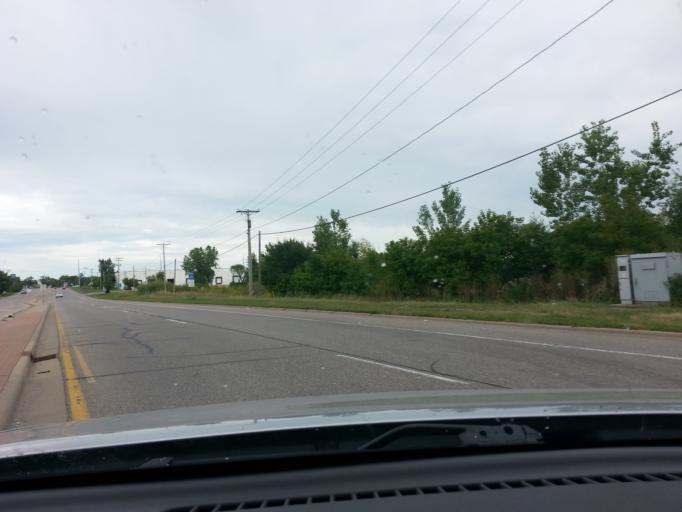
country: US
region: Minnesota
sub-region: Dakota County
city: Lakeville
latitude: 44.6381
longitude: -93.2176
